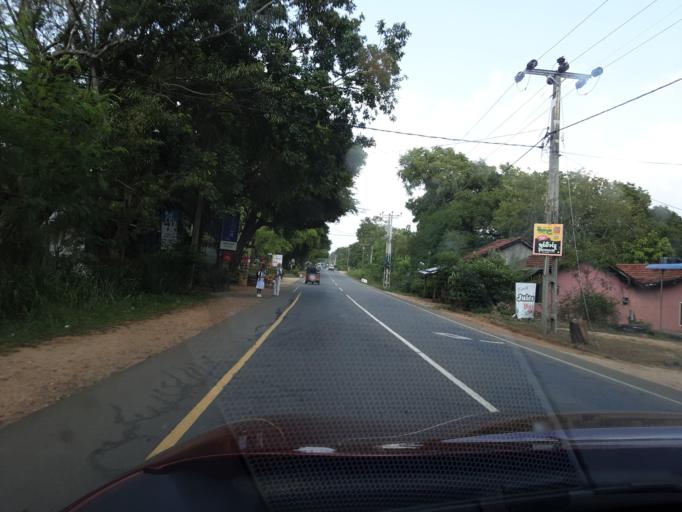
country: LK
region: Uva
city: Haputale
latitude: 6.5283
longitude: 81.1262
